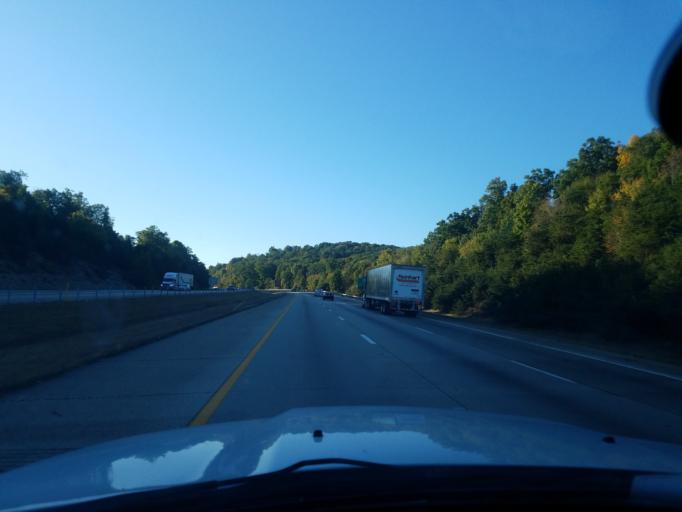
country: US
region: Kentucky
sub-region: Bullitt County
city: Shepherdsville
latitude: 37.9628
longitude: -85.6944
